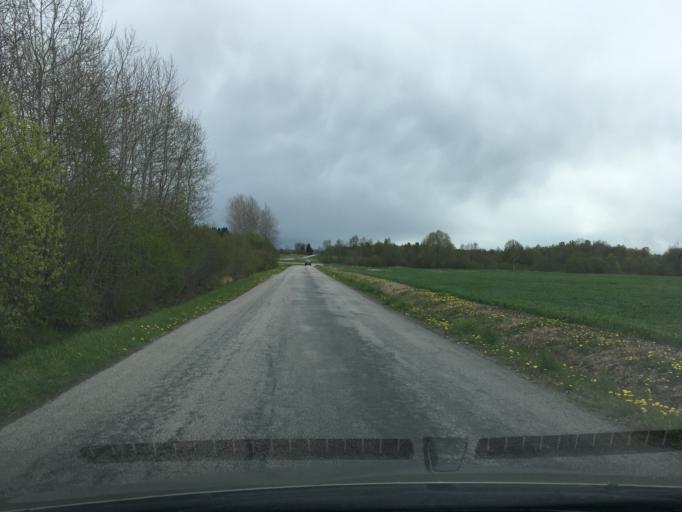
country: EE
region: Harju
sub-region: Joelaehtme vald
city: Loo
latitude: 59.3856
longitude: 24.9658
